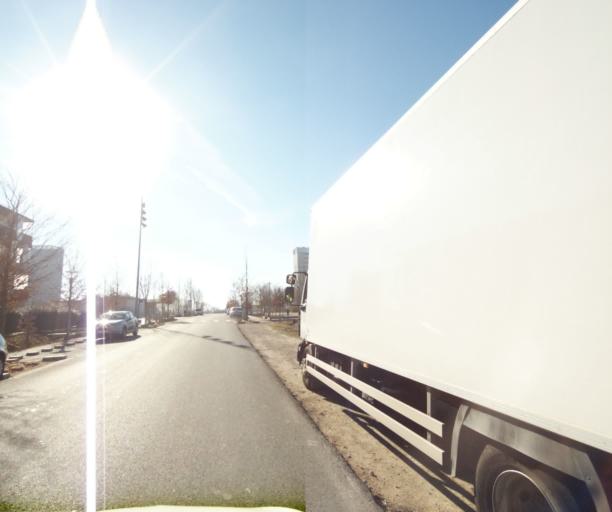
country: FR
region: Lorraine
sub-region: Departement de Meurthe-et-Moselle
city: Maxeville
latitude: 48.7034
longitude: 6.1508
